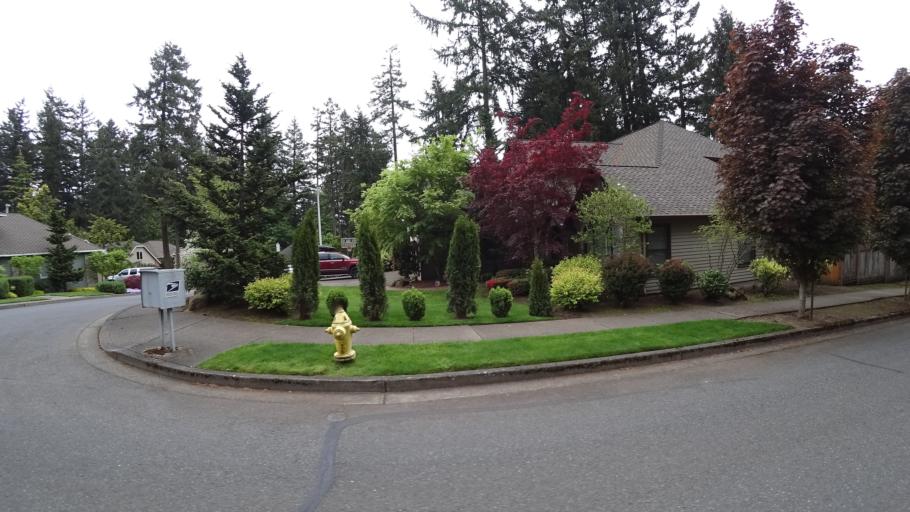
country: US
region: Oregon
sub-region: Washington County
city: Beaverton
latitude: 45.4596
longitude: -122.8204
